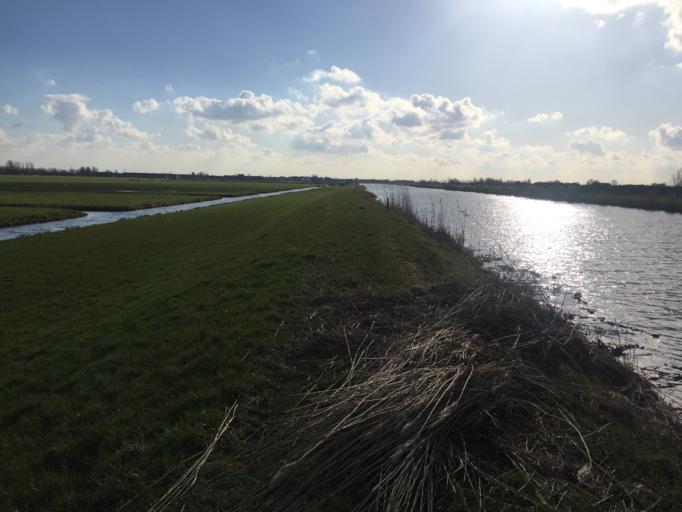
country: NL
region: South Holland
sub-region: Bodegraven-Reeuwijk
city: Bodegraven
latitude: 52.0567
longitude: 4.8025
